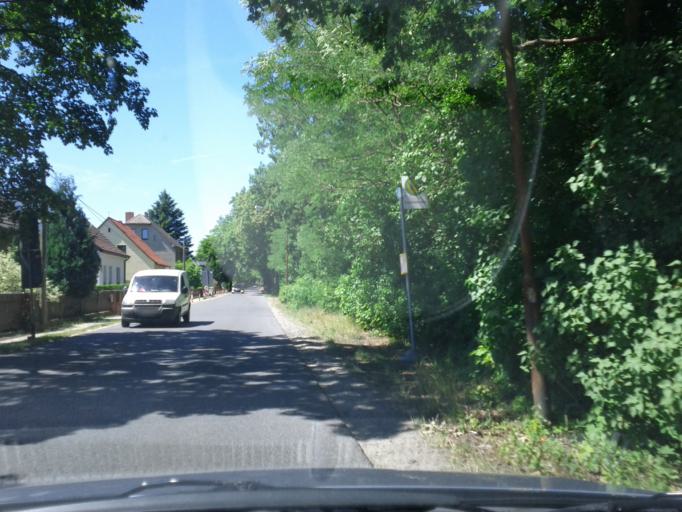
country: DE
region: Brandenburg
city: Furstenwalde
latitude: 52.3389
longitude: 14.0707
